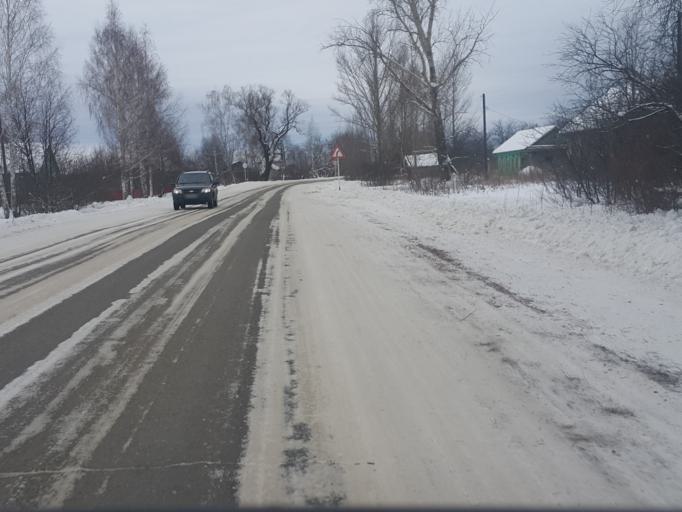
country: RU
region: Tambov
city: Platonovka
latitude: 52.8742
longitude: 41.8726
